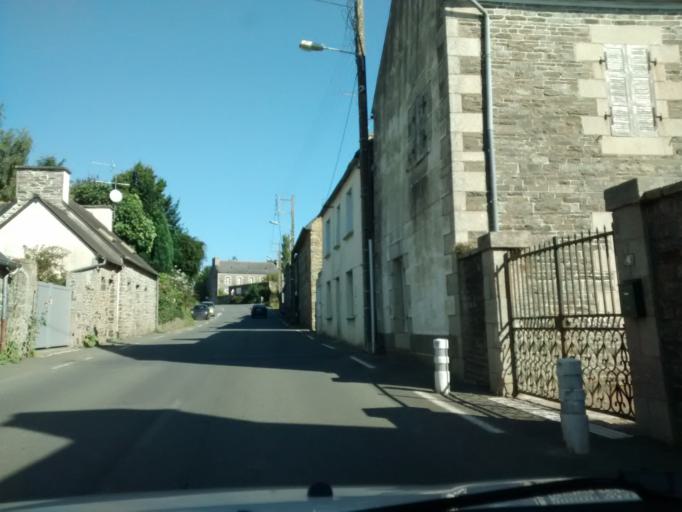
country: FR
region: Brittany
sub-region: Departement des Cotes-d'Armor
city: Tredarzec
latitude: 48.7877
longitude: -3.1987
